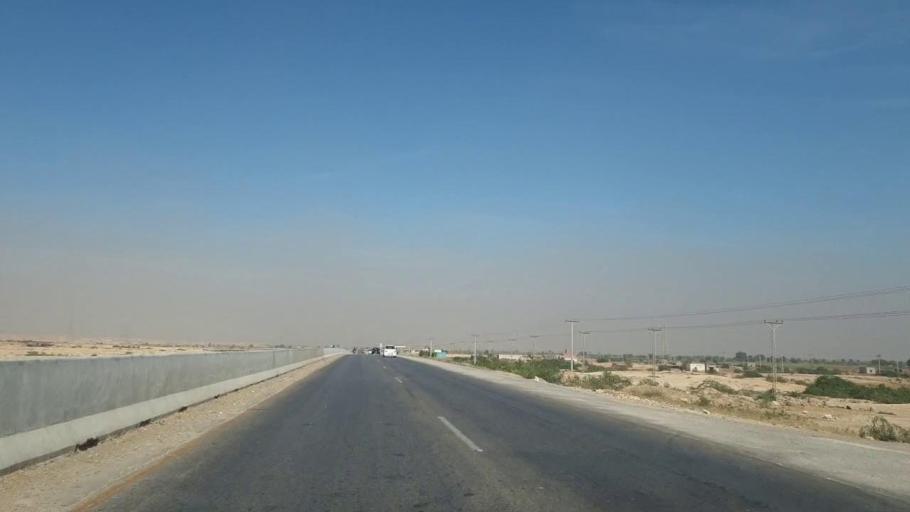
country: PK
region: Sindh
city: Jamshoro
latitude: 25.5073
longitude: 68.2732
